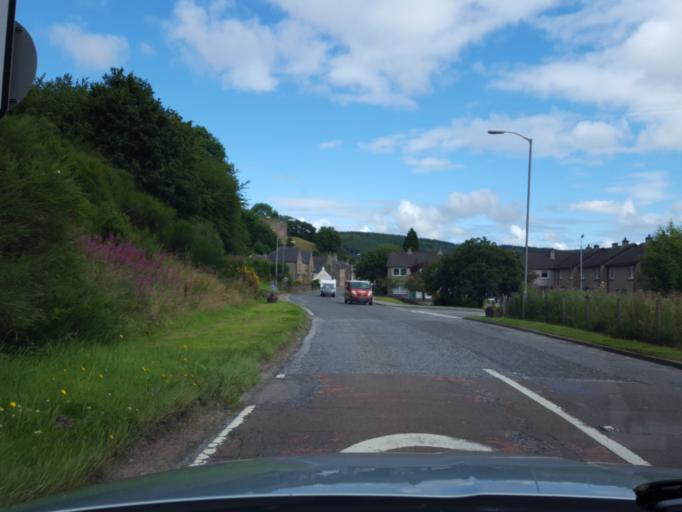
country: GB
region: Scotland
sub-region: Moray
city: Rothes
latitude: 57.5221
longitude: -3.2086
